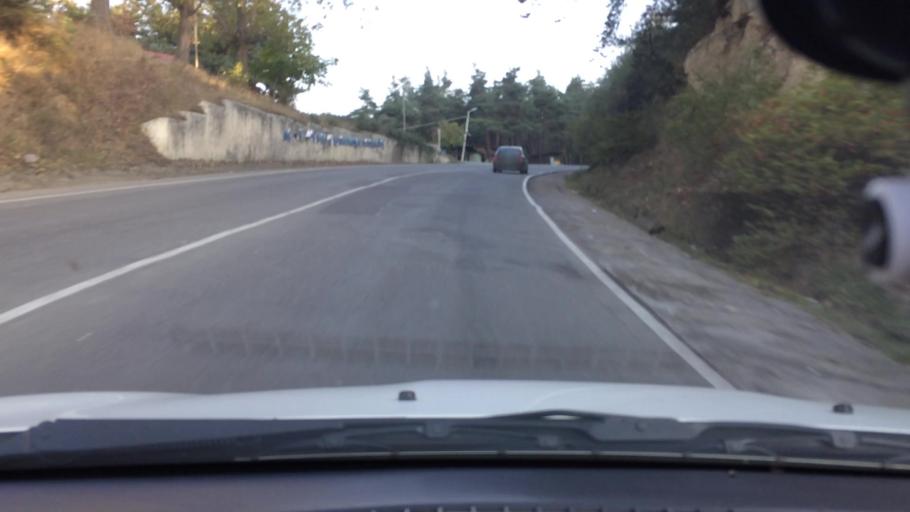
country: GE
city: Surami
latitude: 42.0204
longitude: 43.5656
